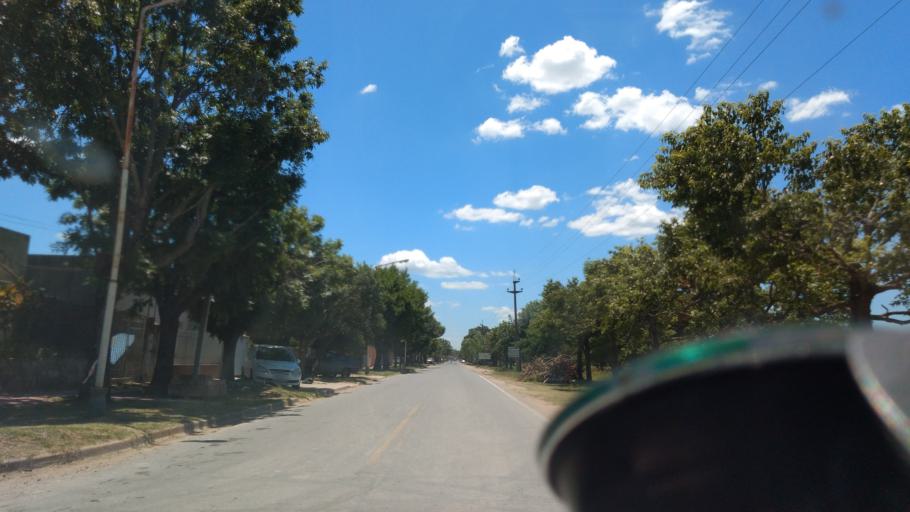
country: AR
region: Santa Fe
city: Laguna Paiva
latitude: -31.3140
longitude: -60.6585
